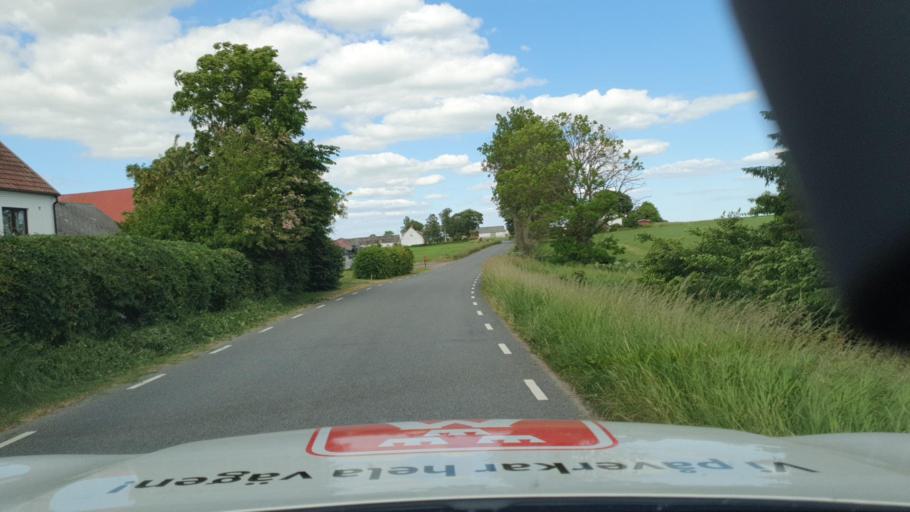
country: SE
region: Skane
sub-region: Ystads Kommun
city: Kopingebro
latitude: 55.4800
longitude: 14.0225
